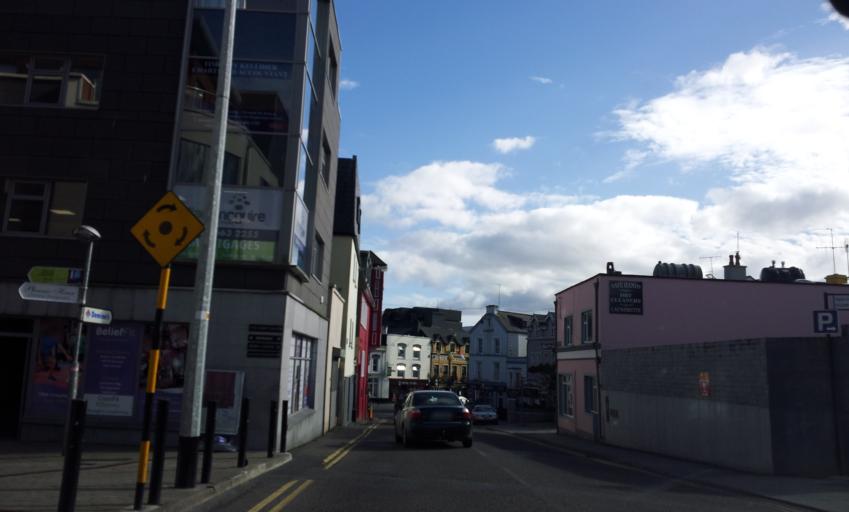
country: IE
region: Munster
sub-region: Ciarrai
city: Cill Airne
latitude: 52.0606
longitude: -9.5061
